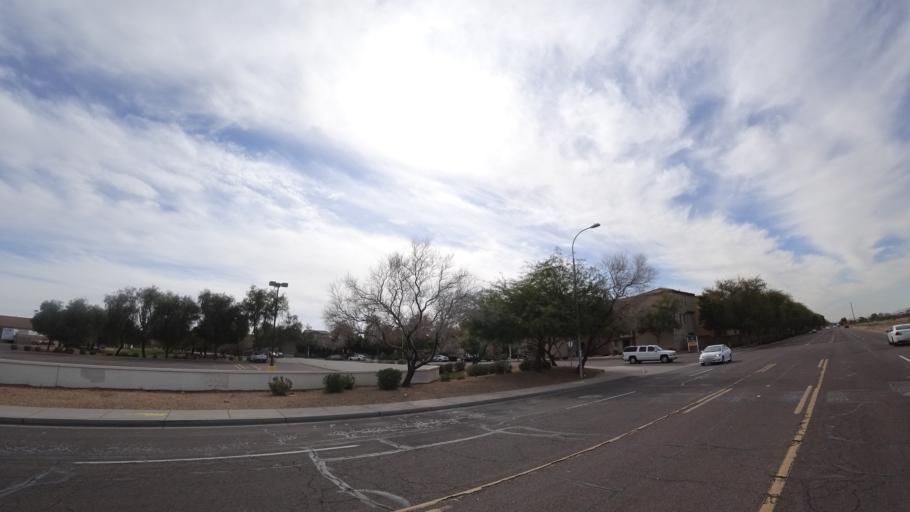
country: US
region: Arizona
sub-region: Maricopa County
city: Tolleson
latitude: 33.4729
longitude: -112.2244
